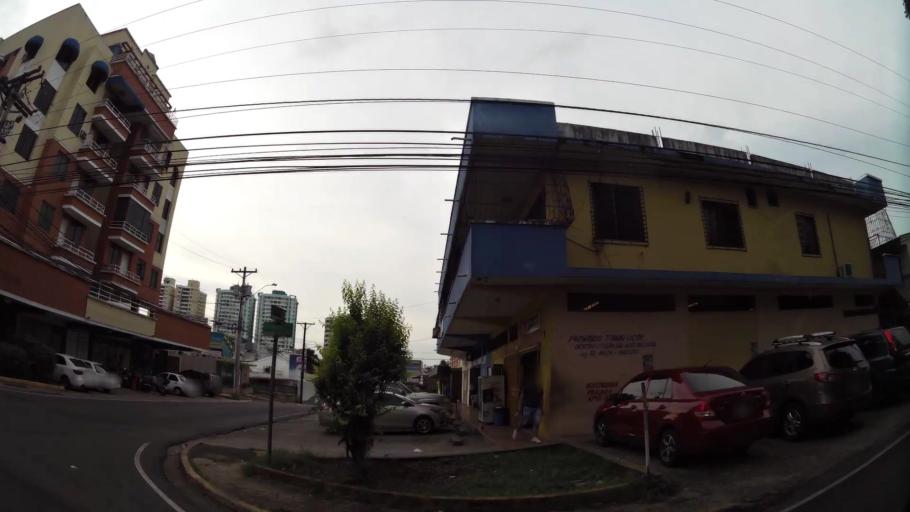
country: PA
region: Panama
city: Panama
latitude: 9.0015
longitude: -79.5142
